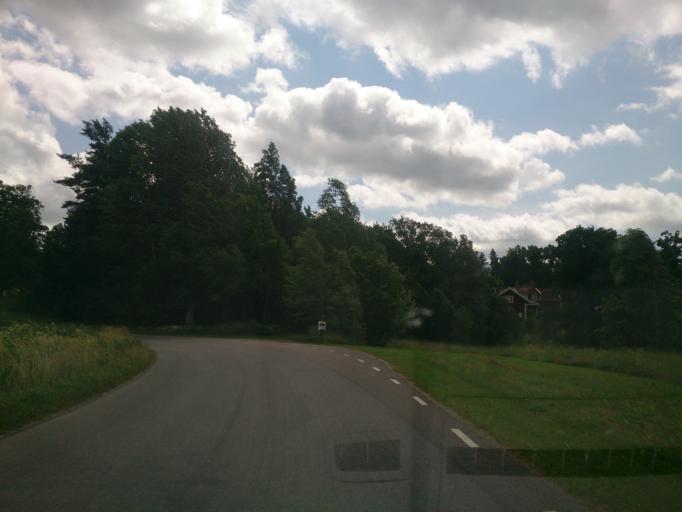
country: SE
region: OEstergoetland
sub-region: Norrkopings Kommun
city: Krokek
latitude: 58.5073
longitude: 16.5396
